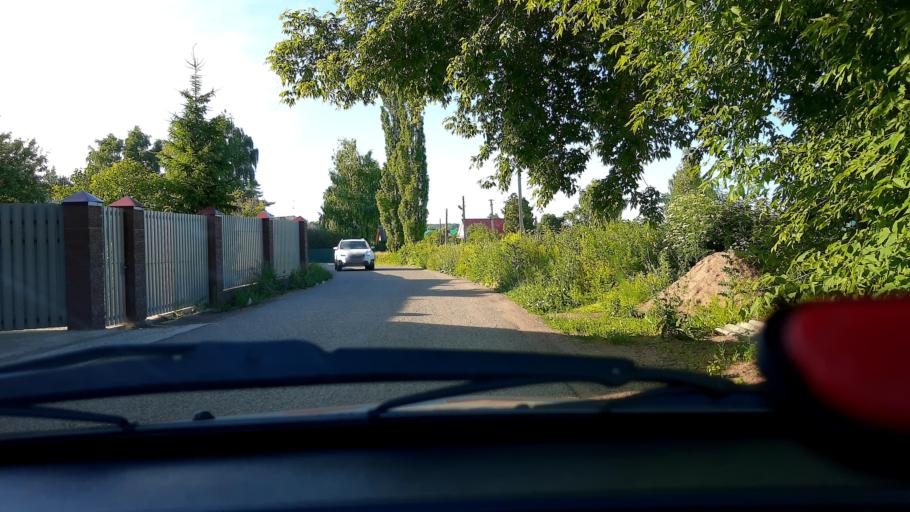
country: RU
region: Bashkortostan
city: Avdon
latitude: 54.4974
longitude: 55.8970
